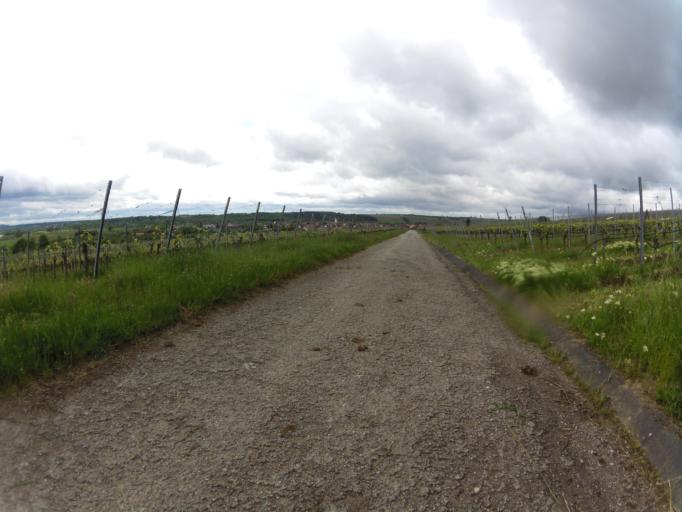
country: DE
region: Bavaria
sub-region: Regierungsbezirk Unterfranken
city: Sommerach
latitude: 49.8360
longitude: 10.2183
